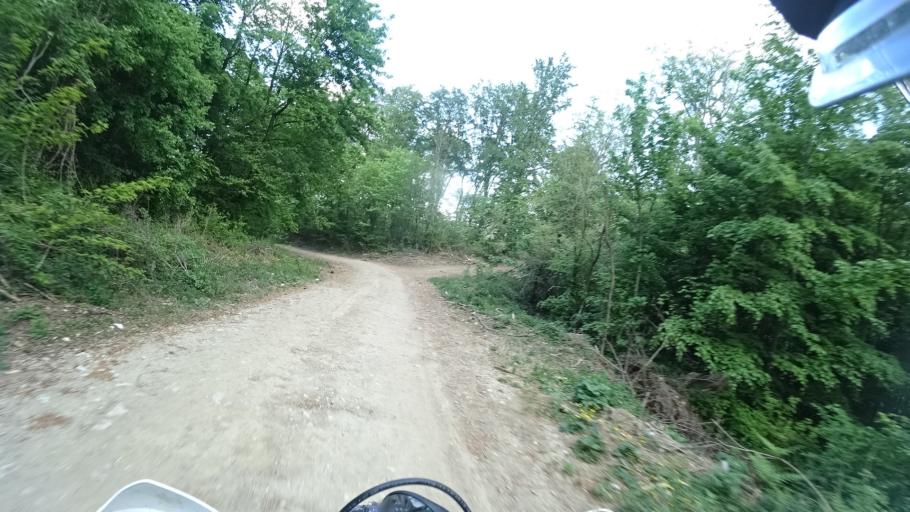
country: HR
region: Zagrebacka
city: Jablanovec
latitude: 45.8534
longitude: 15.8904
